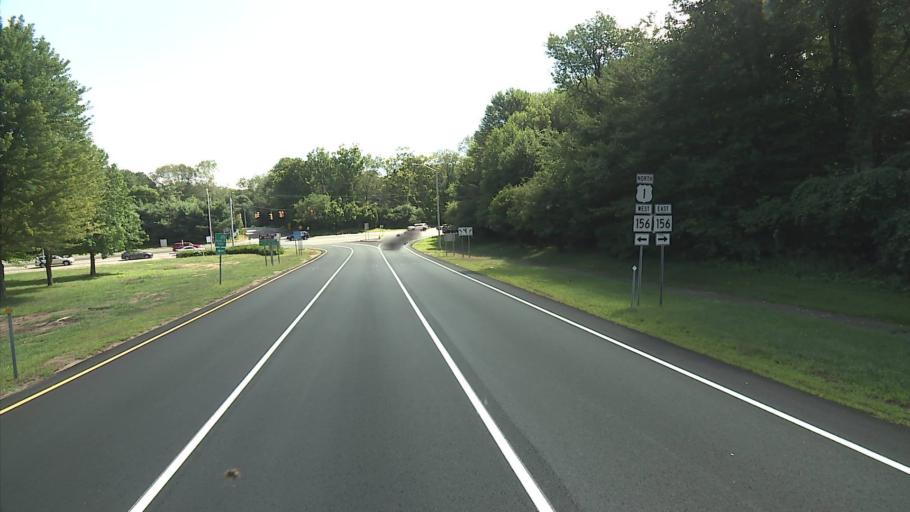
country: US
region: Connecticut
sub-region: Middlesex County
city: Old Saybrook Center
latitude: 41.3196
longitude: -72.3400
